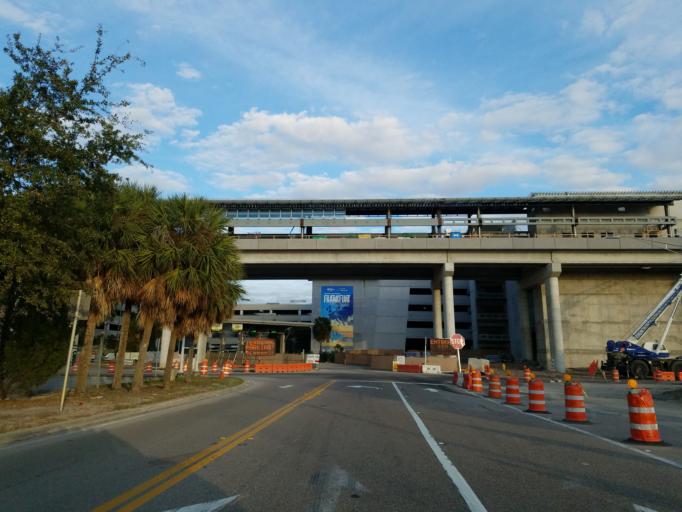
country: US
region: Florida
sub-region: Hillsborough County
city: Egypt Lake-Leto
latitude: 27.9666
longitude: -82.5364
